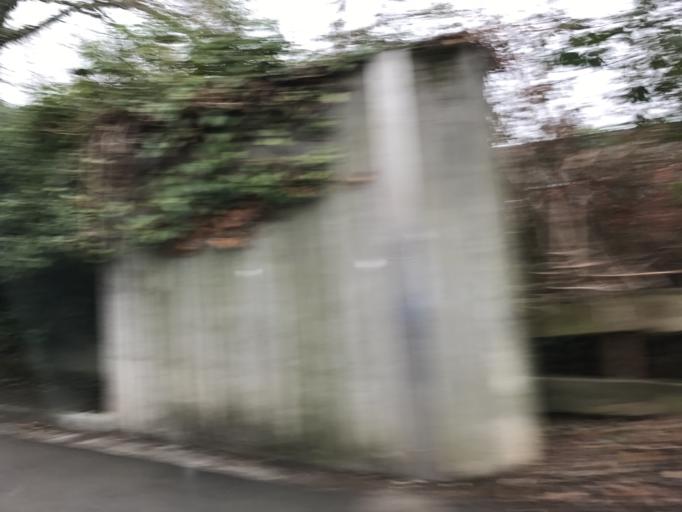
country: DE
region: Hesse
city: Geisenheim
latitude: 49.9669
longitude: 7.9612
